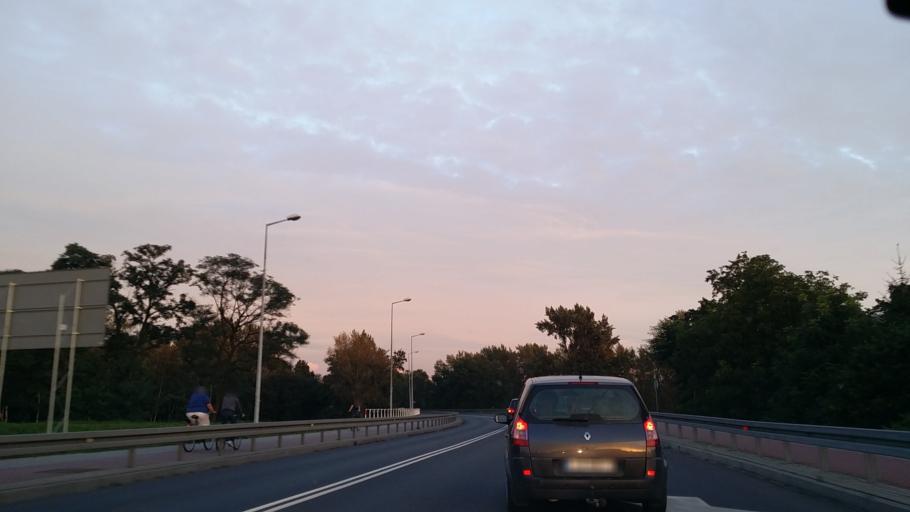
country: PL
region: Lesser Poland Voivodeship
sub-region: Powiat oswiecimski
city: Oswiecim
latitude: 50.0342
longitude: 19.2109
